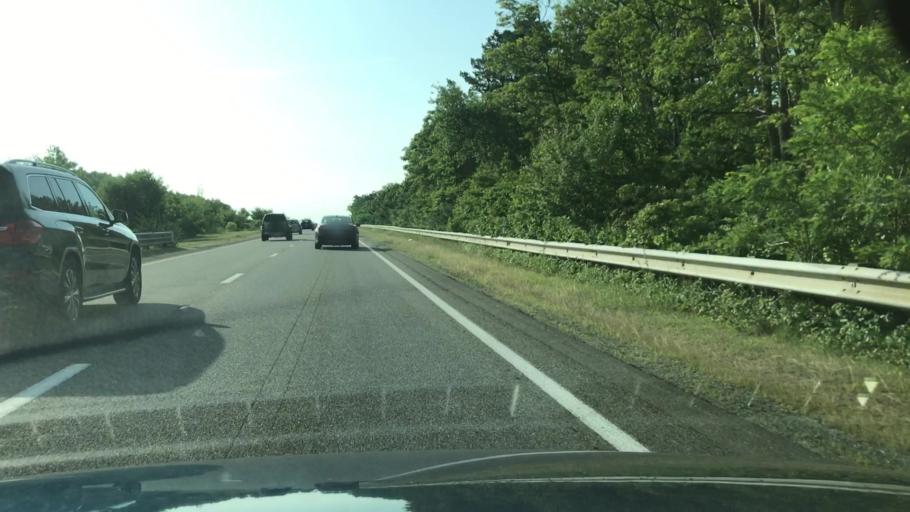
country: US
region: Massachusetts
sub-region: Barnstable County
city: East Sandwich
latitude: 41.7348
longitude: -70.4673
